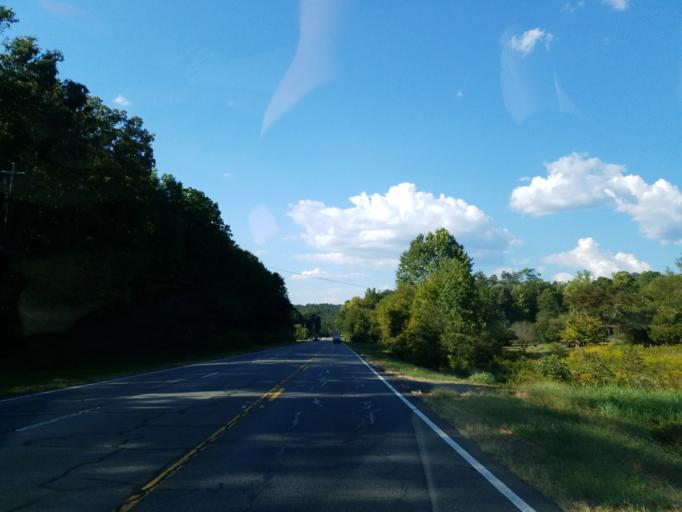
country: US
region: Georgia
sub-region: Bartow County
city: Rydal
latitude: 34.3941
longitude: -84.7074
